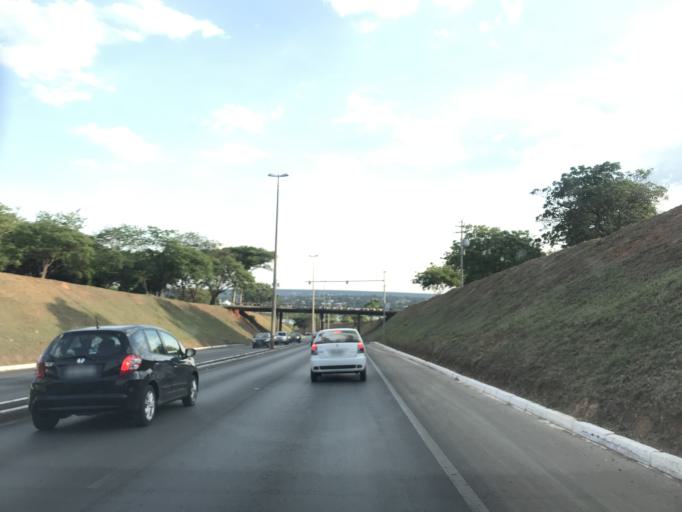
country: BR
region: Federal District
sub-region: Brasilia
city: Brasilia
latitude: -15.8139
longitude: -47.8817
